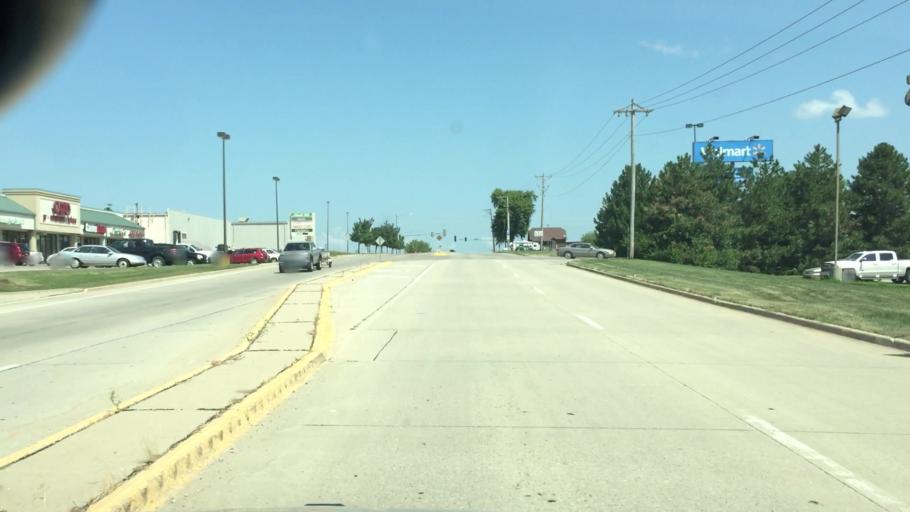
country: US
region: Iowa
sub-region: Jasper County
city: Newton
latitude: 41.6966
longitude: -93.0144
